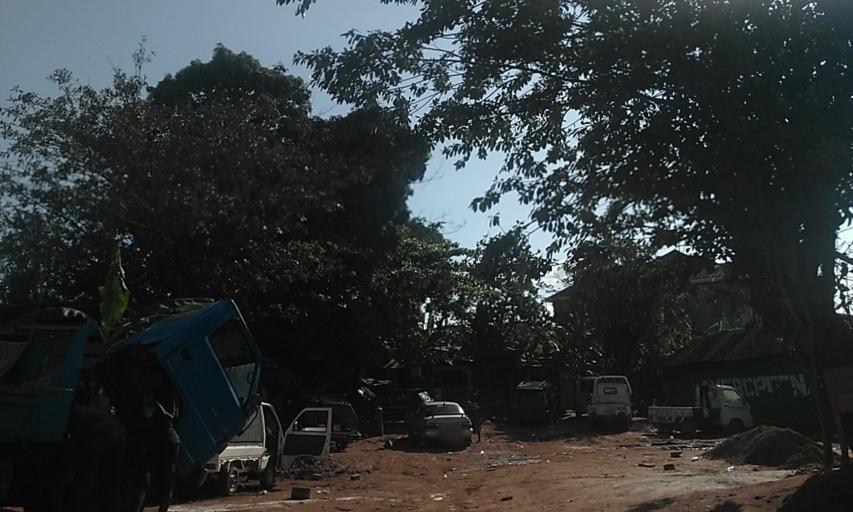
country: UG
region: Central Region
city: Kampala Central Division
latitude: 0.3269
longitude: 32.5363
